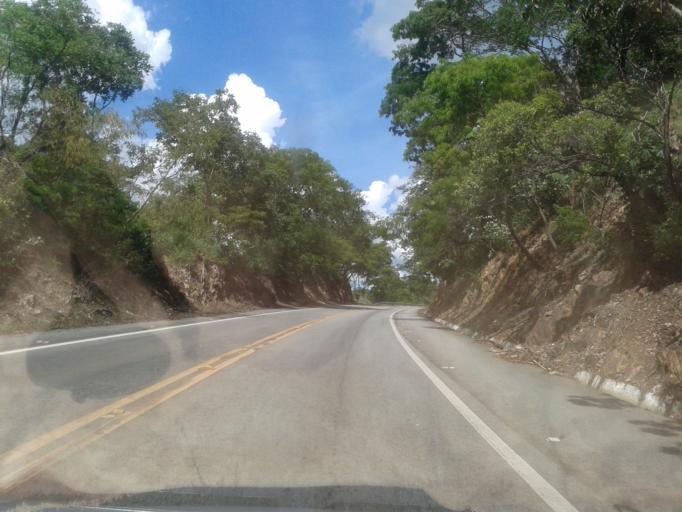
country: BR
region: Goias
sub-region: Goias
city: Goias
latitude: -15.9245
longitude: -50.1360
